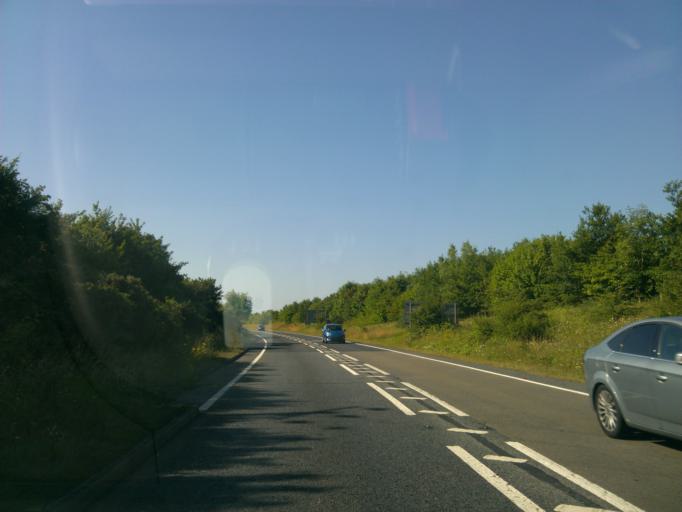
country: GB
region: England
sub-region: Essex
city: Great Bentley
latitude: 51.8591
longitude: 1.1016
